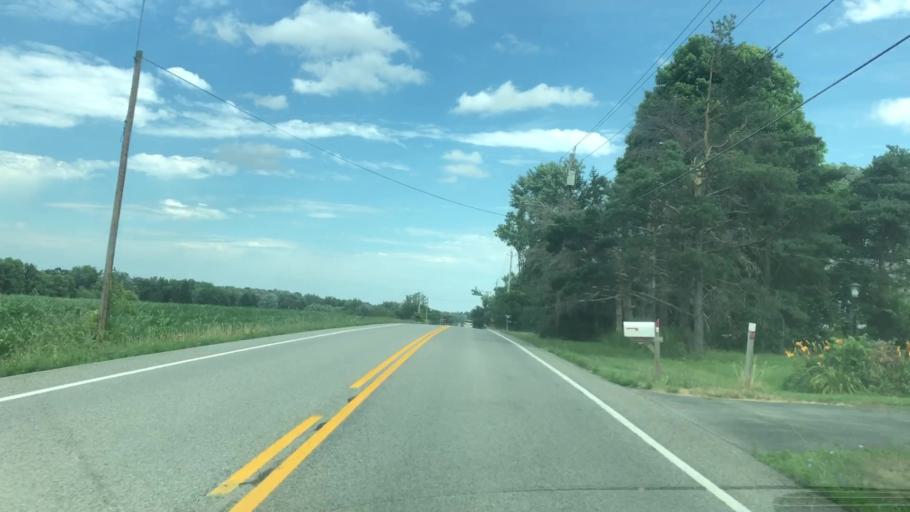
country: US
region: New York
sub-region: Wayne County
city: Macedon
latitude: 43.1026
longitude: -77.3522
